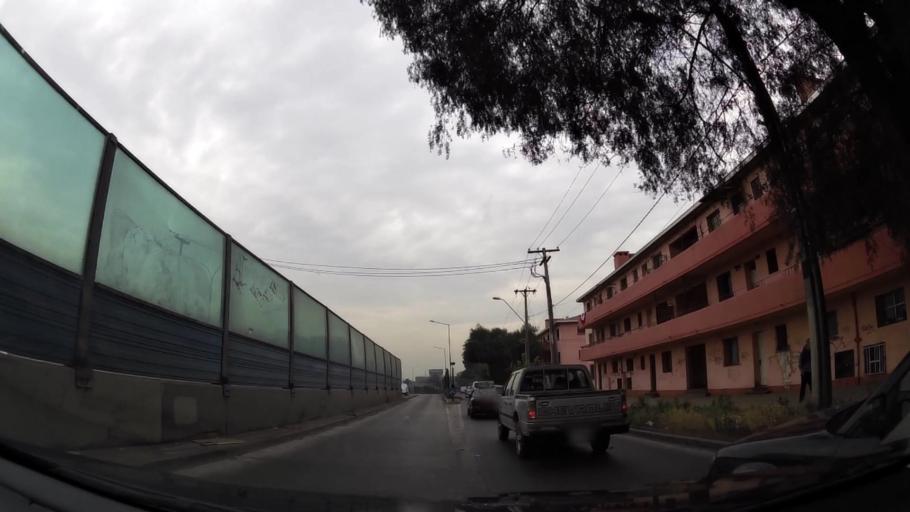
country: CL
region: Santiago Metropolitan
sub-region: Provincia de Santiago
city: Santiago
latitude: -33.4211
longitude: -70.6751
